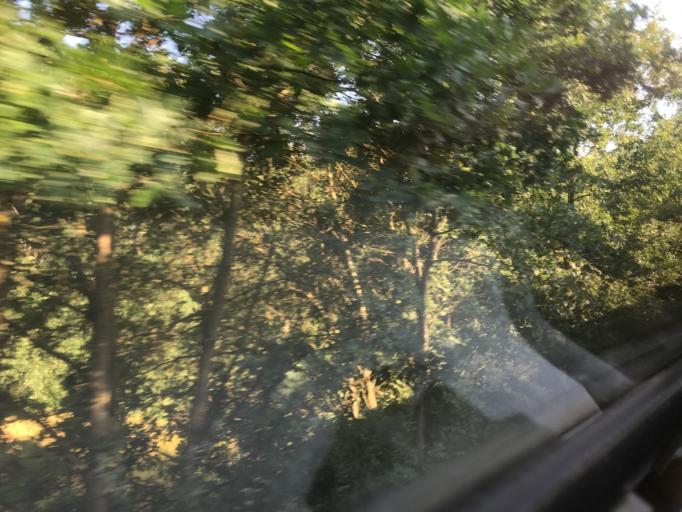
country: CZ
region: Jihocesky
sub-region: Okres Jindrichuv Hradec
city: Lomnice nad Luznici
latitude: 49.1207
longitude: 14.7368
